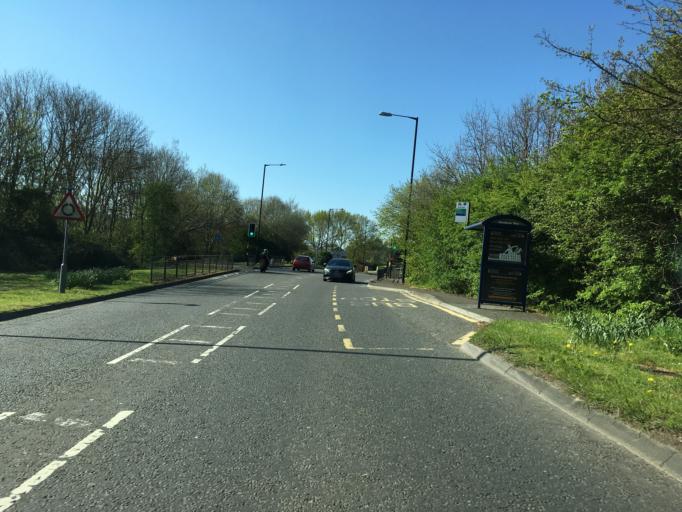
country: GB
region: England
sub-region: North Somerset
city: Portishead
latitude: 51.4804
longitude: -2.7589
